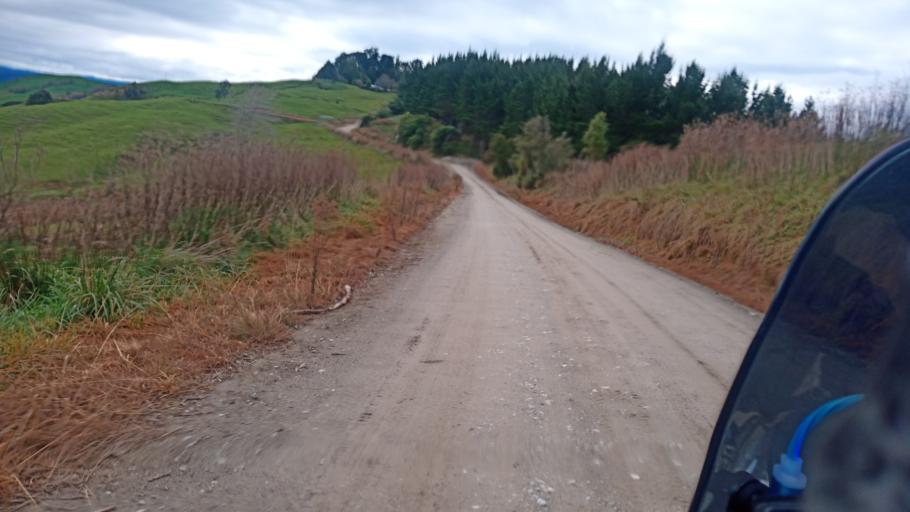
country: NZ
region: Gisborne
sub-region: Gisborne District
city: Gisborne
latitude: -38.3752
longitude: 177.9679
